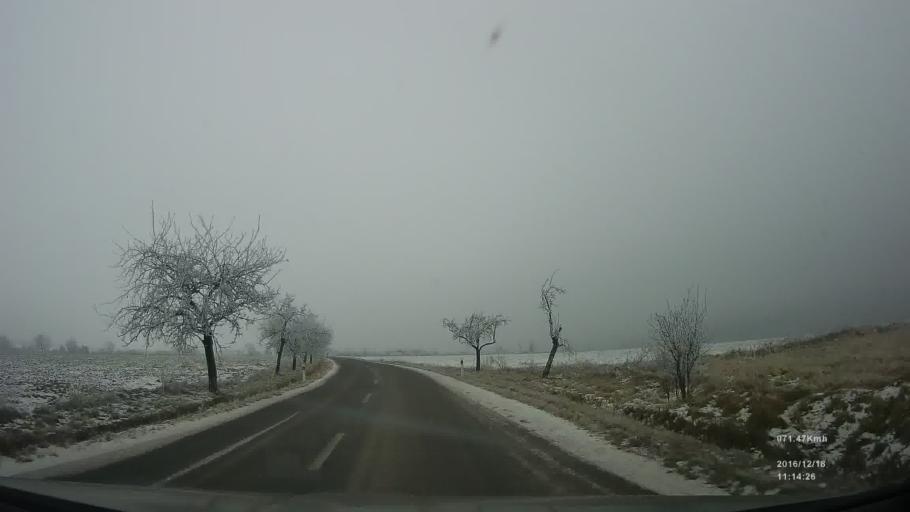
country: SK
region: Presovsky
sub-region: Okres Presov
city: Presov
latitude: 48.8935
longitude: 21.3172
